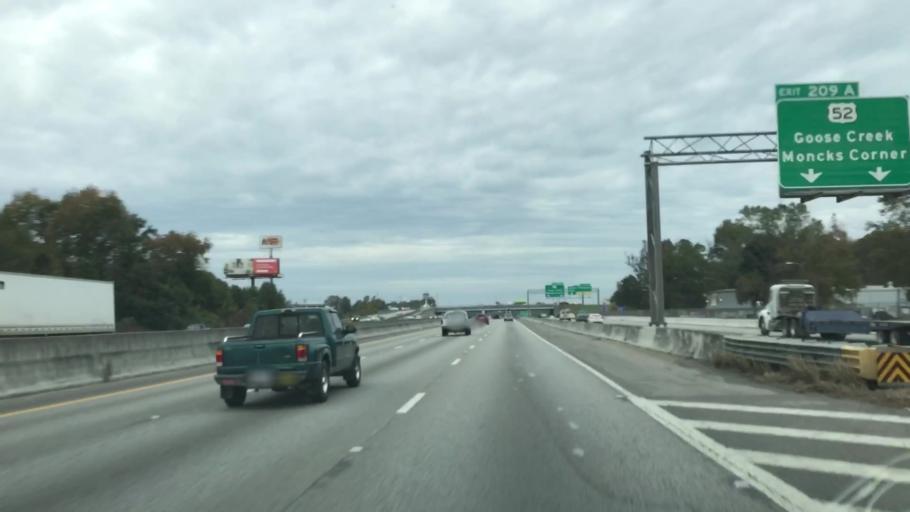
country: US
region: South Carolina
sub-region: Berkeley County
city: Hanahan
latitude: 32.9311
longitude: -80.0454
